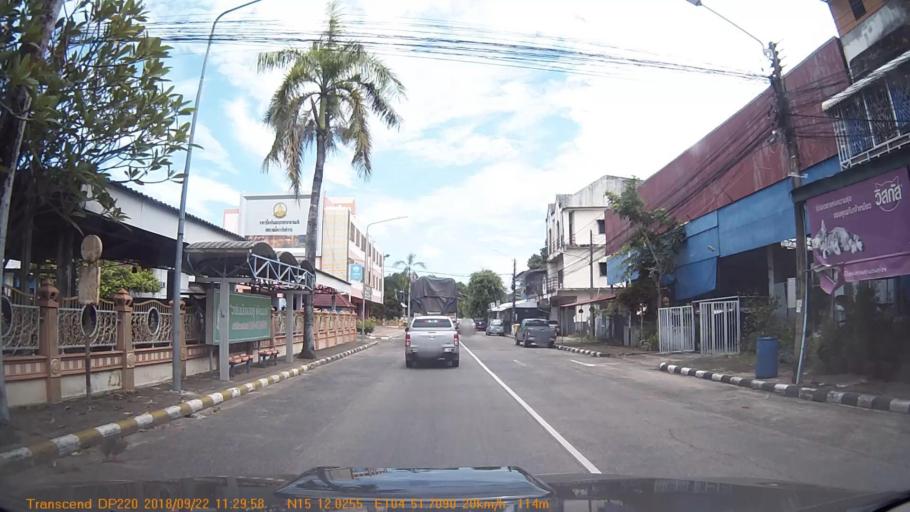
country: TH
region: Changwat Ubon Ratchathani
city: Warin Chamrap
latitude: 15.2005
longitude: 104.8619
